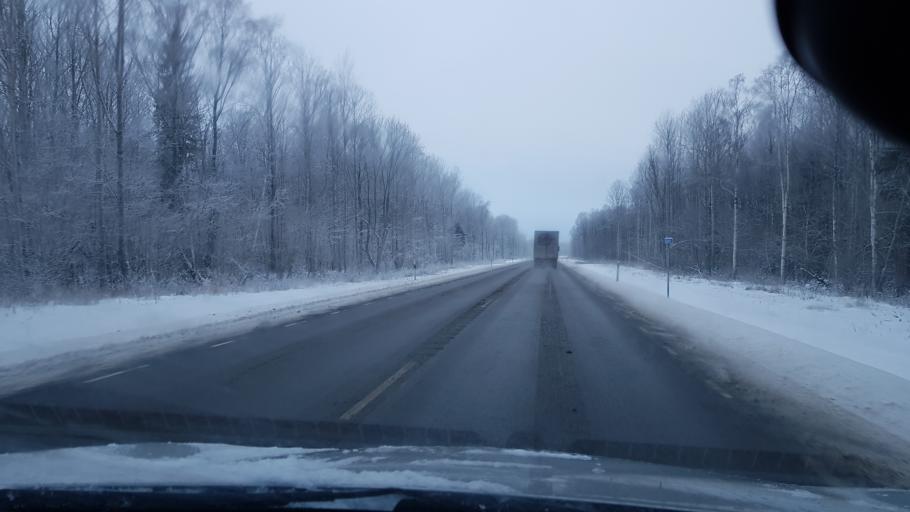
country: EE
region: Harju
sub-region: Paldiski linn
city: Paldiski
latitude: 59.3398
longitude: 24.1337
